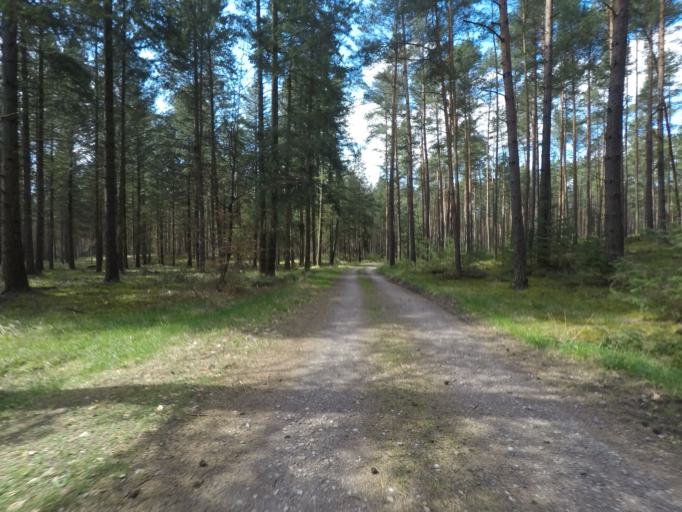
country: DE
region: Brandenburg
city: Melchow
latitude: 52.8229
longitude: 13.6727
